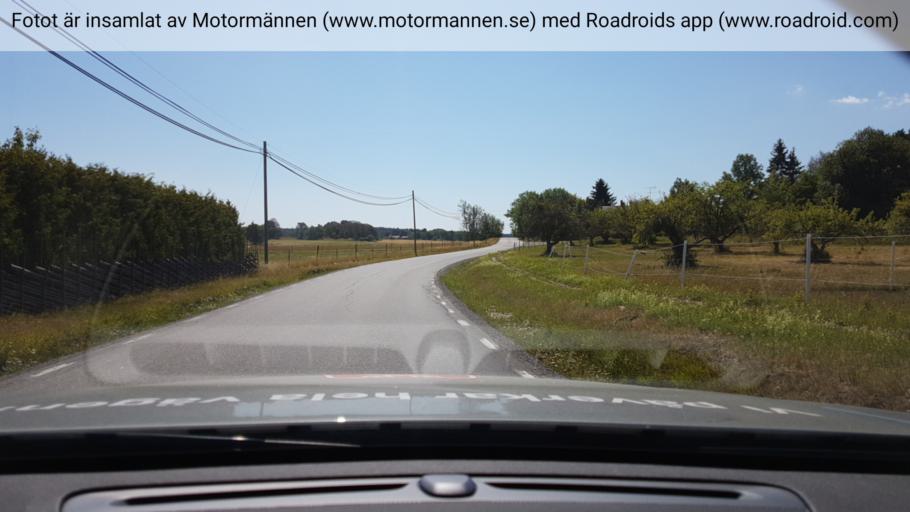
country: SE
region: Stockholm
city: Stenhamra
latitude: 59.4018
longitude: 17.6572
